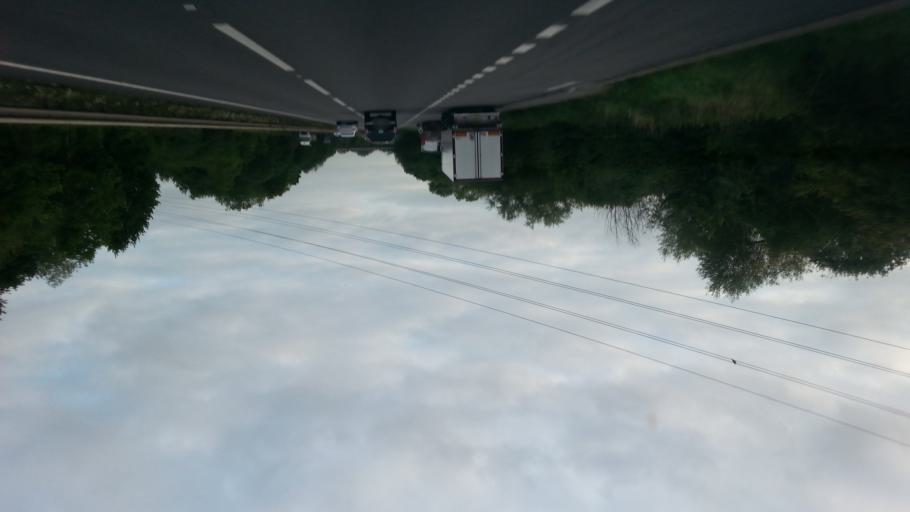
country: GB
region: England
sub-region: Northamptonshire
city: Brackley
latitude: 52.0343
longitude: -1.1341
